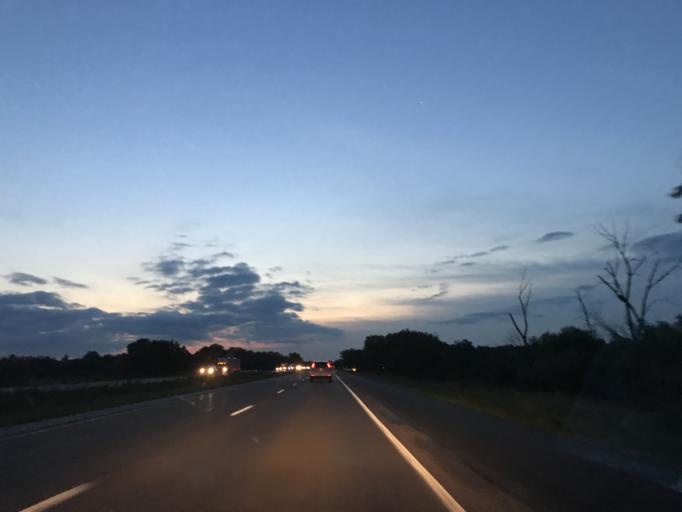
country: US
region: Iowa
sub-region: Jasper County
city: Colfax
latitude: 41.6965
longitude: -93.2253
